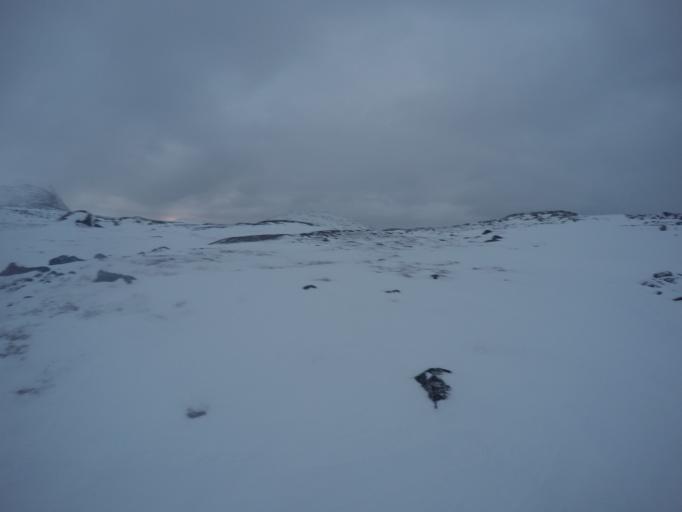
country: GL
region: Sermersooq
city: Nuuk
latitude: 64.1376
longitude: -51.6754
